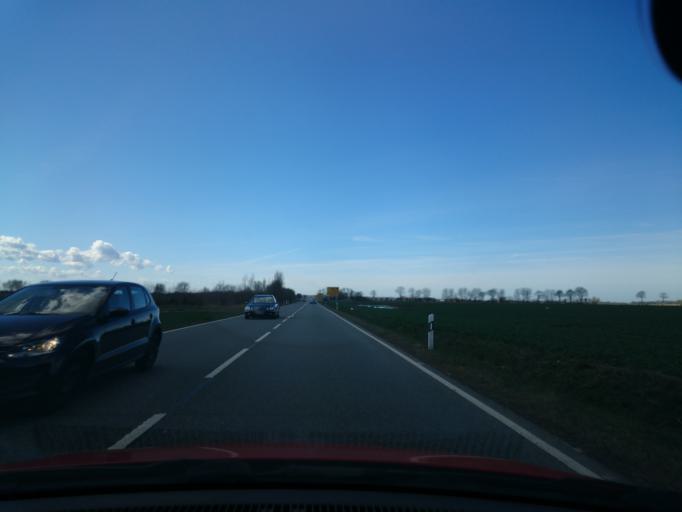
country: DE
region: Mecklenburg-Vorpommern
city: Trinwillershagen
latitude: 54.2899
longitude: 12.6407
